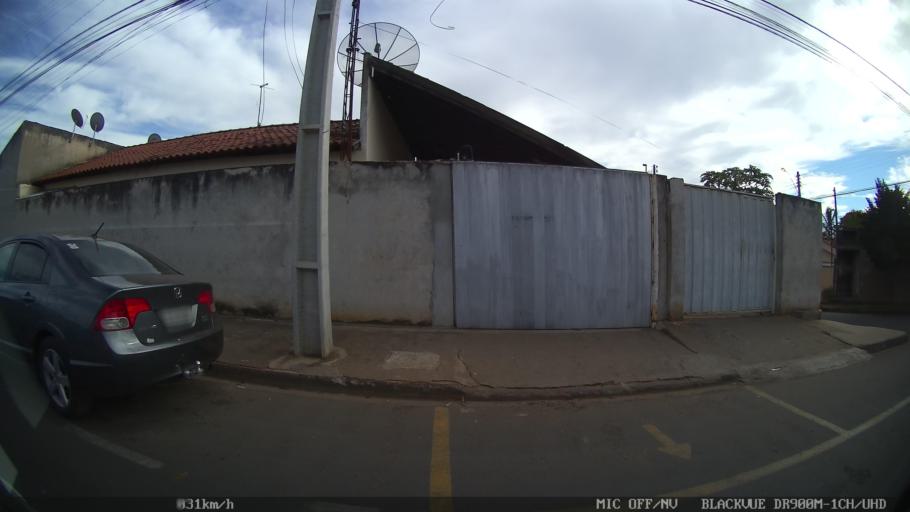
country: BR
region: Sao Paulo
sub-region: Catanduva
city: Catanduva
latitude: -21.1407
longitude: -49.0030
